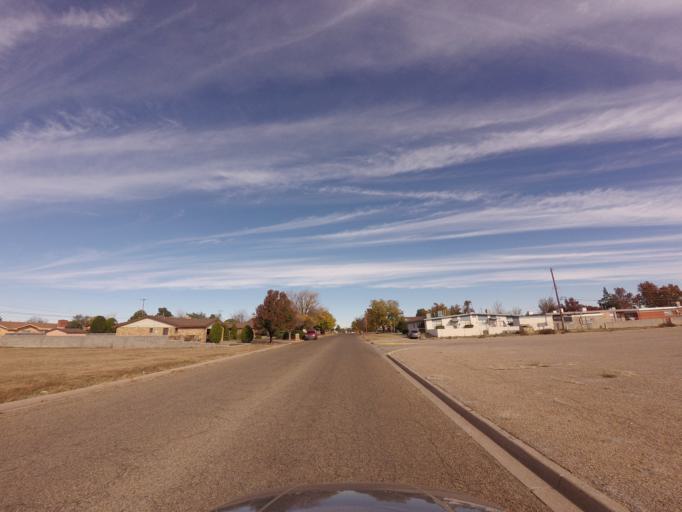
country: US
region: New Mexico
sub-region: Curry County
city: Clovis
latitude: 34.4202
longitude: -103.2255
